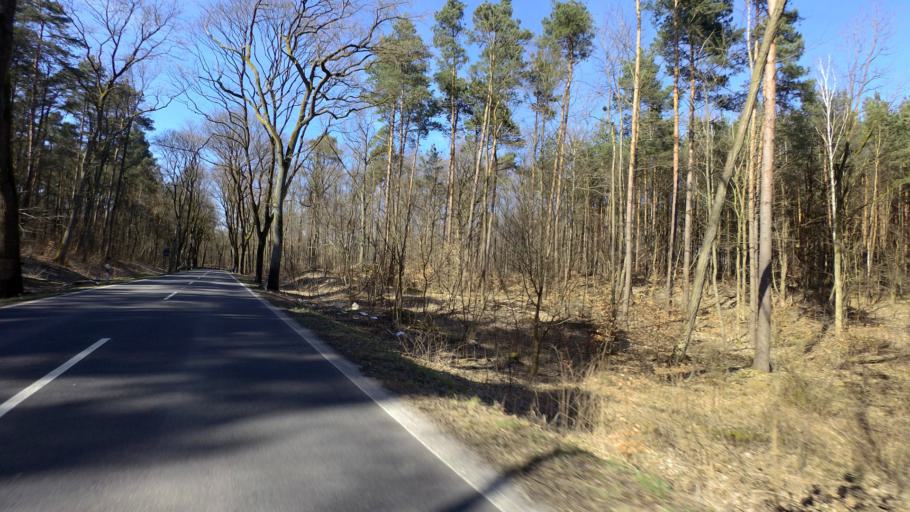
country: DE
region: Brandenburg
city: Waldsieversdorf
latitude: 52.5345
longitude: 14.0633
